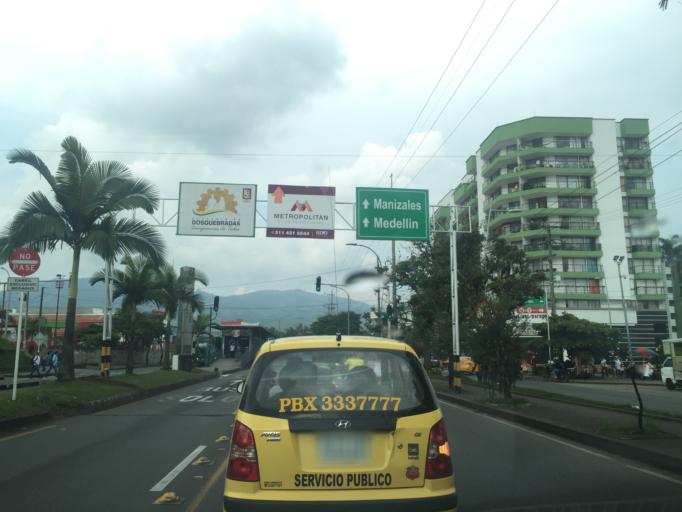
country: CO
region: Risaralda
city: Pereira
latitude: 4.8224
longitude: -75.6838
